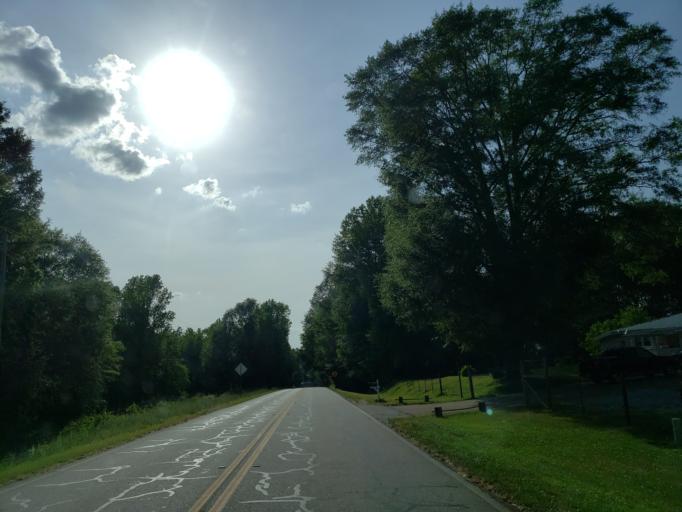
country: US
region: Georgia
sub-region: Carroll County
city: Bowdon
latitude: 33.4738
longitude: -85.2862
